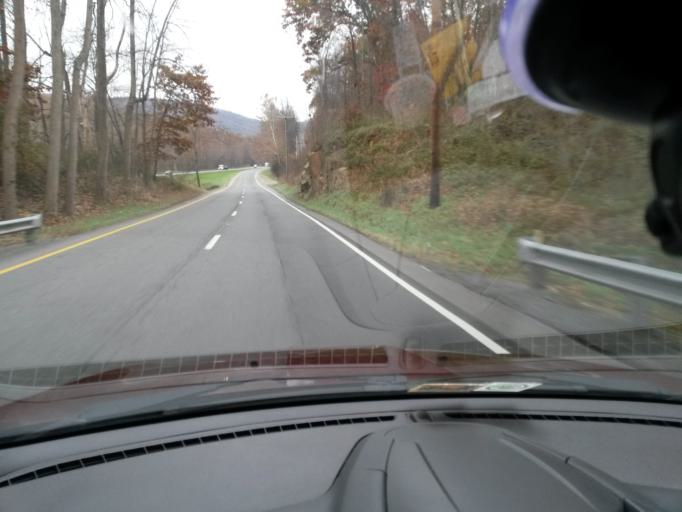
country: US
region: Virginia
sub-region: Albemarle County
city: Crozet
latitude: 37.9080
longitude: -78.6916
